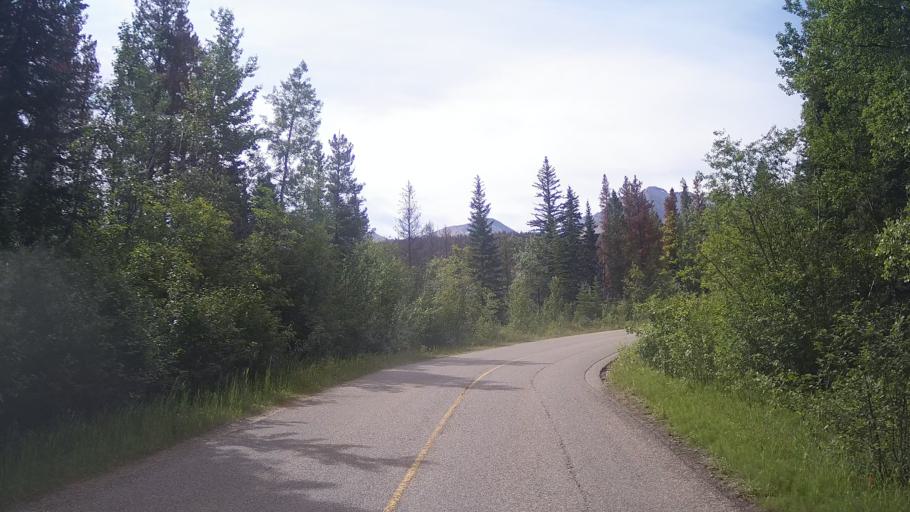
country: CA
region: Alberta
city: Hinton
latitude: 53.1780
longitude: -117.8404
